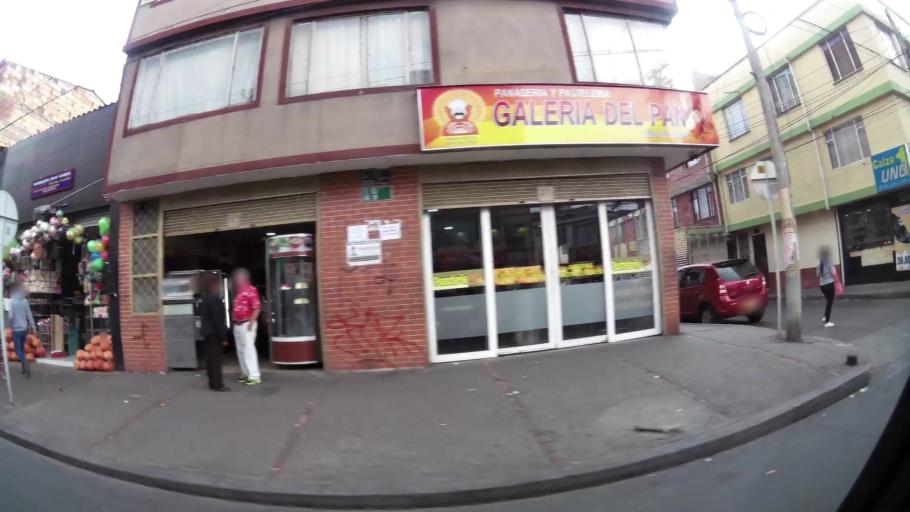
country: CO
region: Cundinamarca
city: La Calera
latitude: 4.7403
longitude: -74.0308
